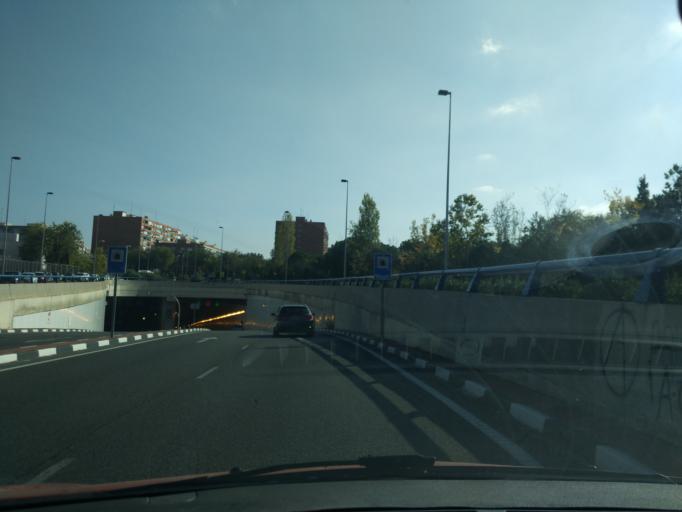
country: ES
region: Madrid
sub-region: Provincia de Madrid
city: Tetuan de las Victorias
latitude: 40.4847
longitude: -3.7163
